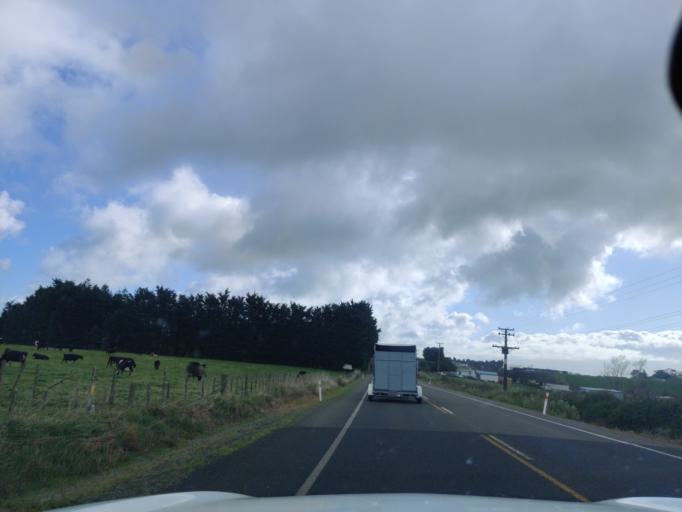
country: NZ
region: Manawatu-Wanganui
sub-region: Palmerston North City
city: Palmerston North
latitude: -40.4383
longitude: 175.5592
